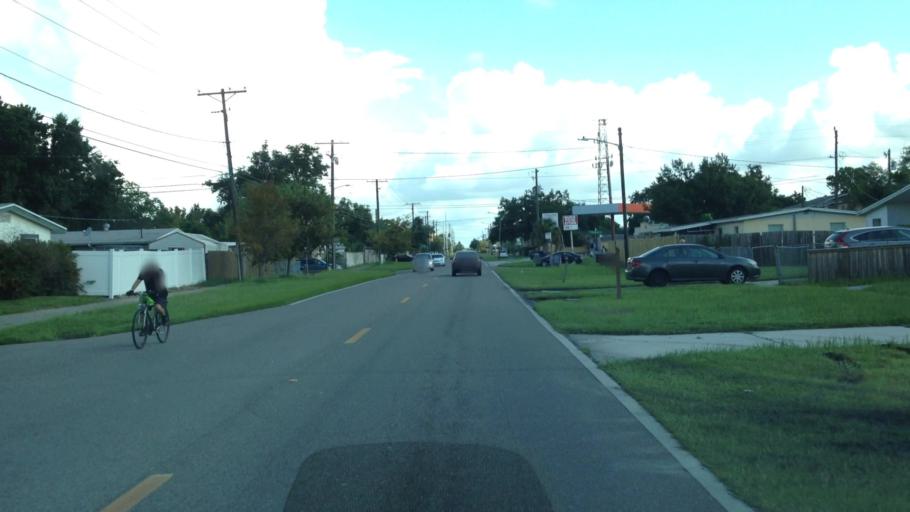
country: US
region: Florida
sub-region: Hillsborough County
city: Tampa
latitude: 27.8831
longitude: -82.5184
